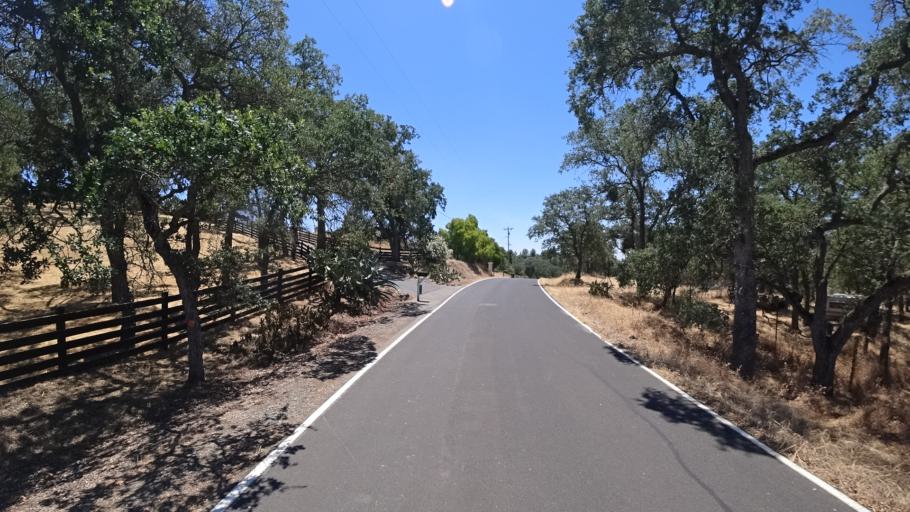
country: US
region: California
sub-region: Calaveras County
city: Rancho Calaveras
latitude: 38.1296
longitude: -120.8492
